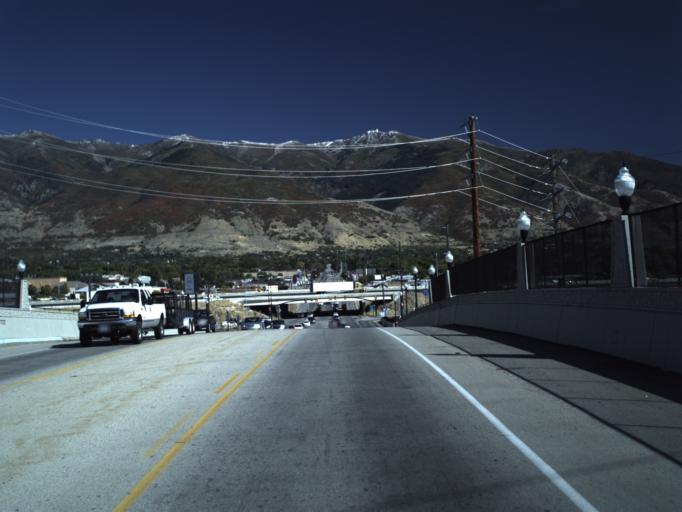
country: US
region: Utah
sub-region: Davis County
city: Kaysville
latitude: 41.0382
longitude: -111.9528
